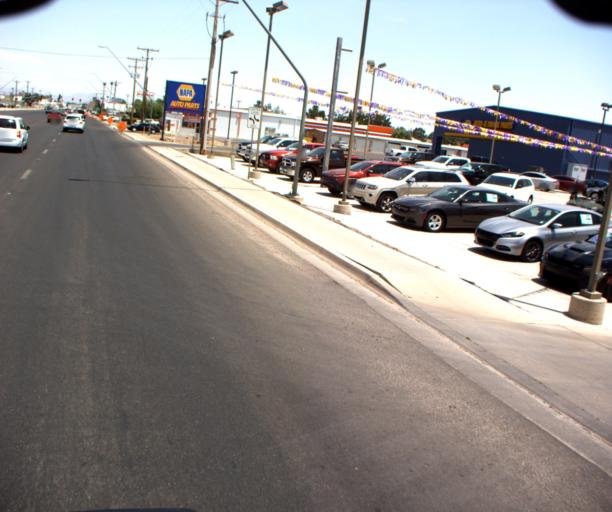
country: US
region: Arizona
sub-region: Graham County
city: Safford
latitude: 32.8349
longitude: -109.7279
